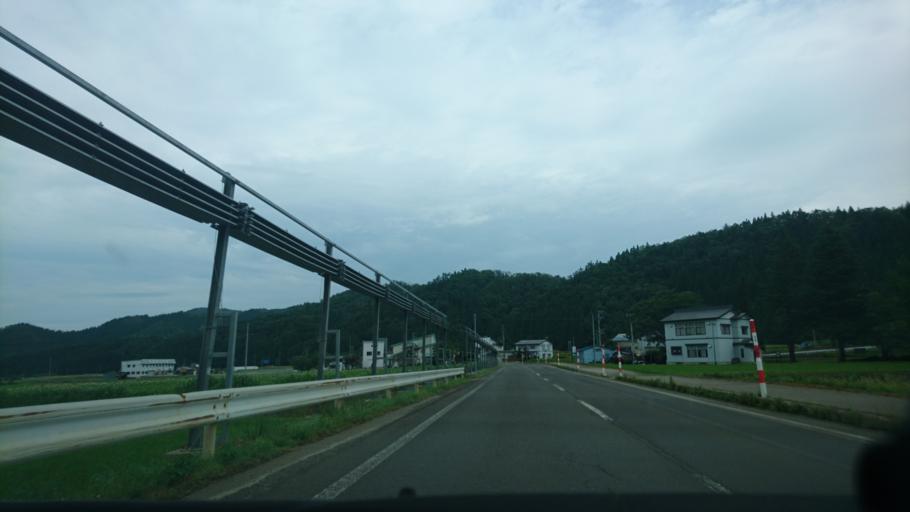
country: JP
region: Akita
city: Yuzawa
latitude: 39.1915
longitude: 140.6186
